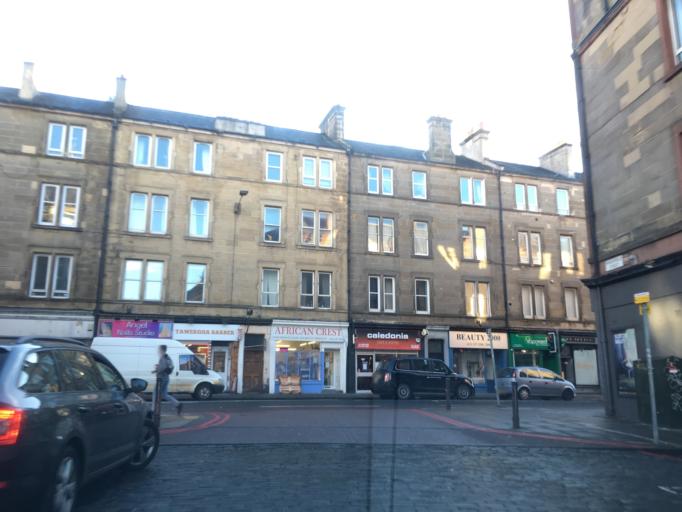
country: GB
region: Scotland
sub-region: Edinburgh
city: Colinton
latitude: 55.9378
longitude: -3.2337
